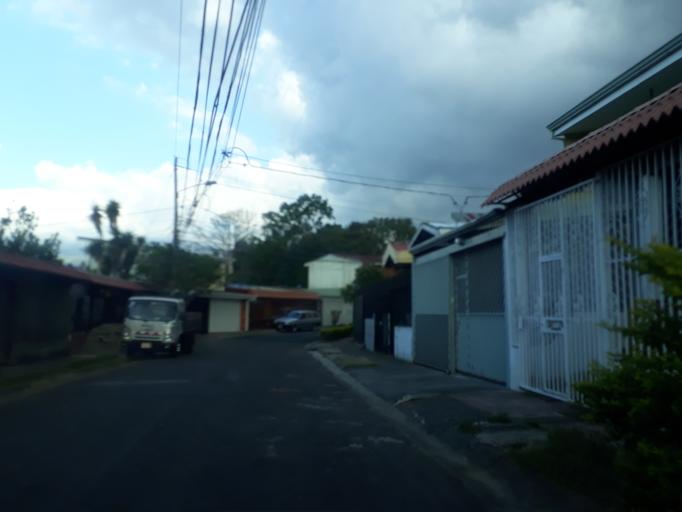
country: CR
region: San Jose
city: Purral
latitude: 9.9548
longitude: -84.0358
